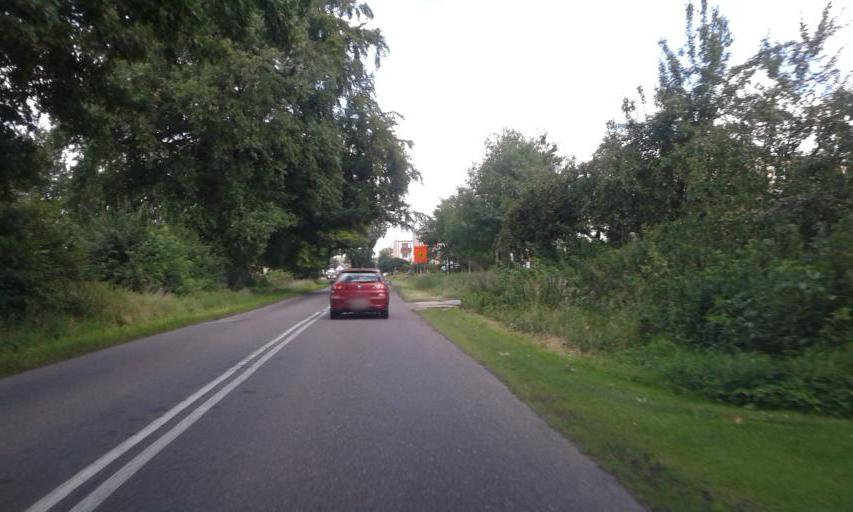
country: PL
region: West Pomeranian Voivodeship
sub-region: Powiat slawienski
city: Slawno
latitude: 54.2722
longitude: 16.6730
